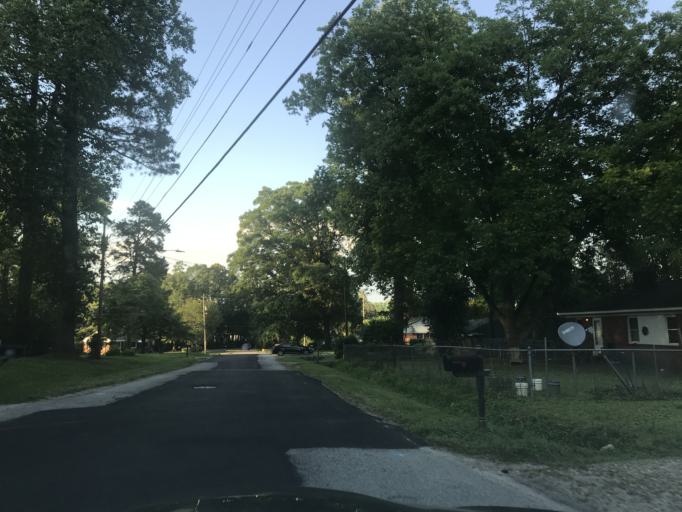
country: US
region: North Carolina
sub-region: Wake County
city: Raleigh
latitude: 35.7505
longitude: -78.6609
